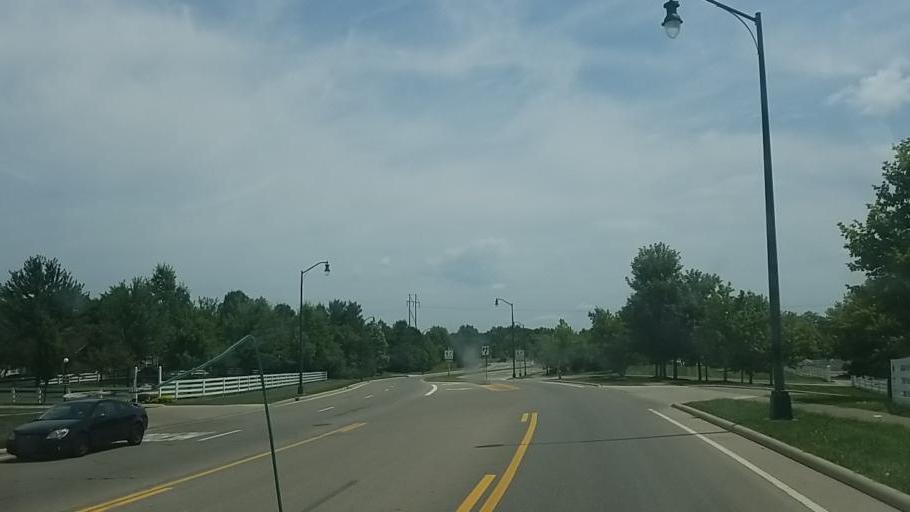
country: US
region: Ohio
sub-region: Franklin County
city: New Albany
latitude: 40.0545
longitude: -82.8443
